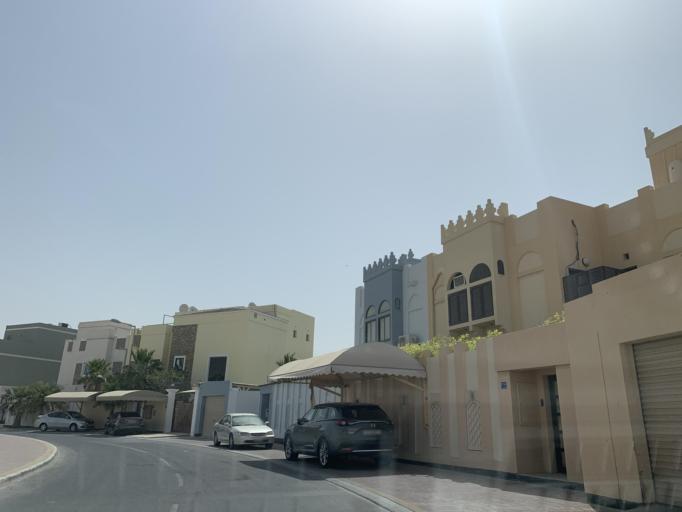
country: BH
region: Northern
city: Madinat `Isa
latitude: 26.1682
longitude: 50.5199
